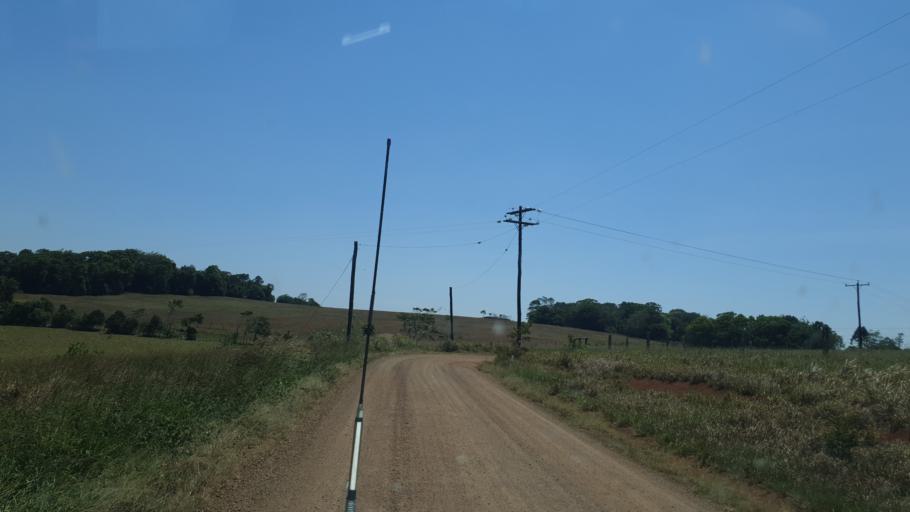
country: AU
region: Queensland
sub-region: Tablelands
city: Atherton
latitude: -17.3496
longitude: 145.6214
